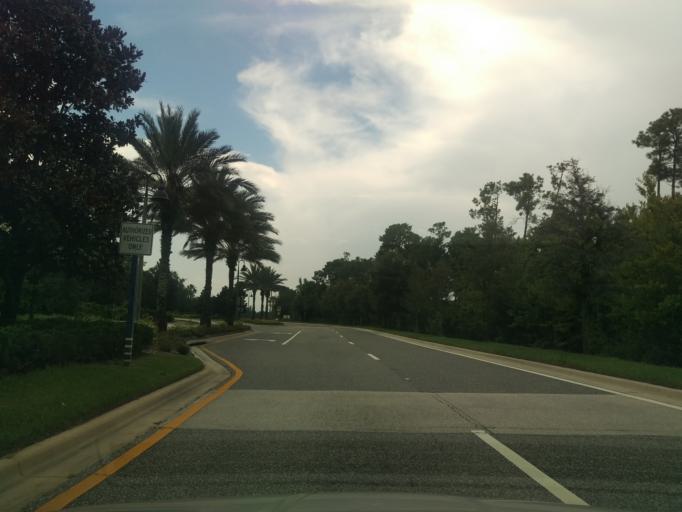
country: US
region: Florida
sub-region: Osceola County
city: Celebration
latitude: 28.3597
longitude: -81.5405
